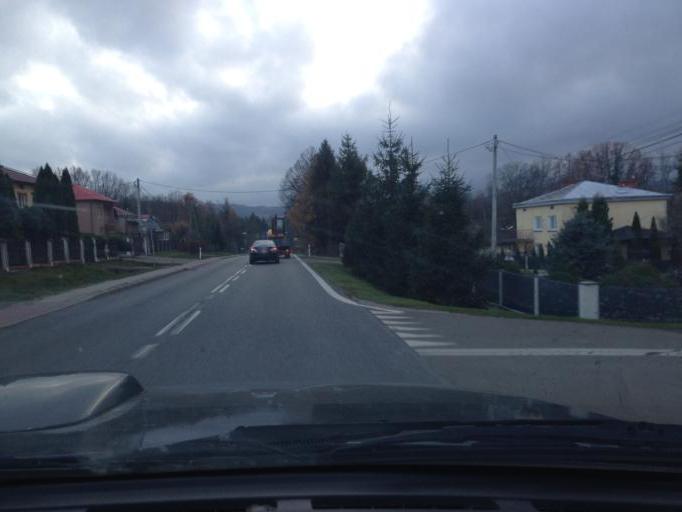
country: PL
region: Subcarpathian Voivodeship
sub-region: Powiat jasielski
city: Nowy Zmigrod
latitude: 49.6136
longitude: 21.5330
